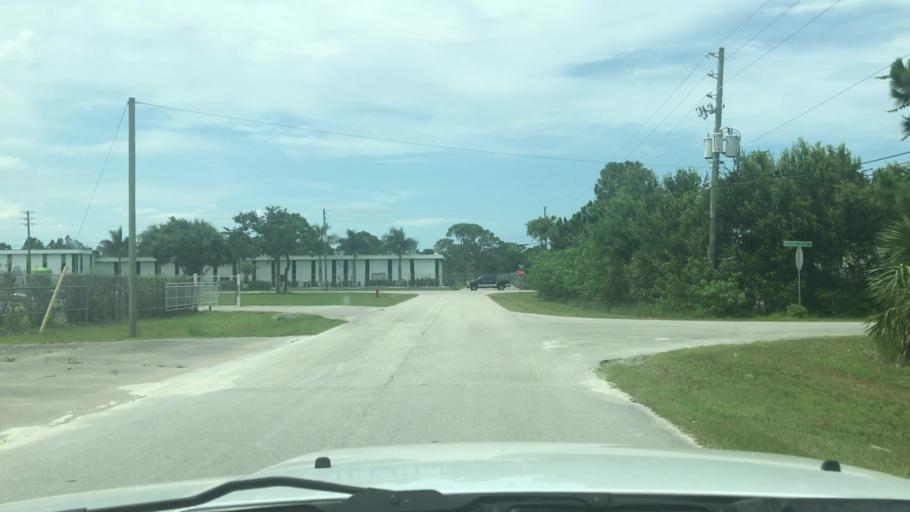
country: US
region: Florida
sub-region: Saint Lucie County
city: Fort Pierce North
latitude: 27.4928
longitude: -80.3517
